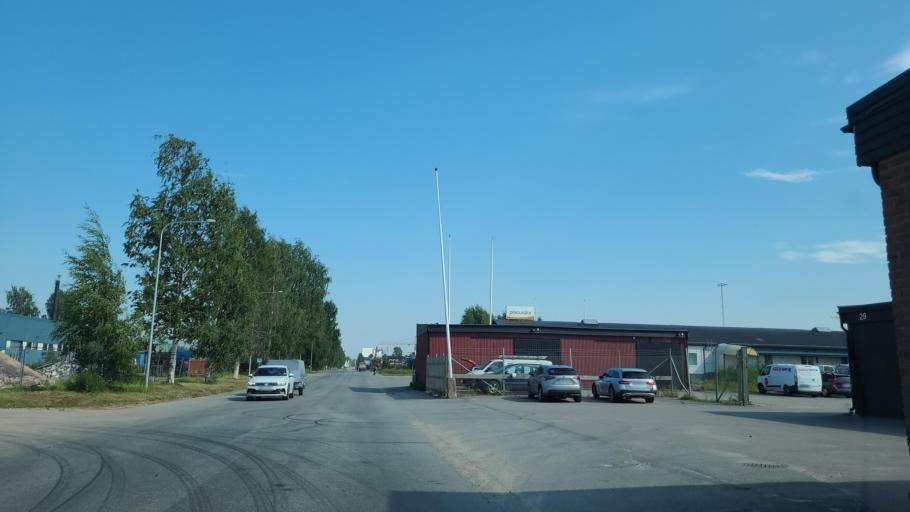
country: SE
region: Vaesterbotten
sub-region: Umea Kommun
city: Roback
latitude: 63.8460
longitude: 20.2147
